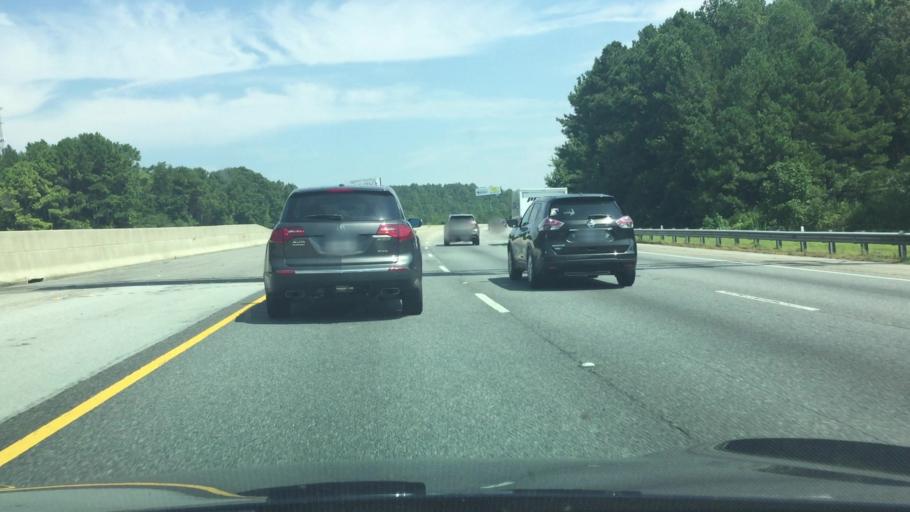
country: US
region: Alabama
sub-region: Shelby County
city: Pelham
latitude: 33.3179
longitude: -86.7869
